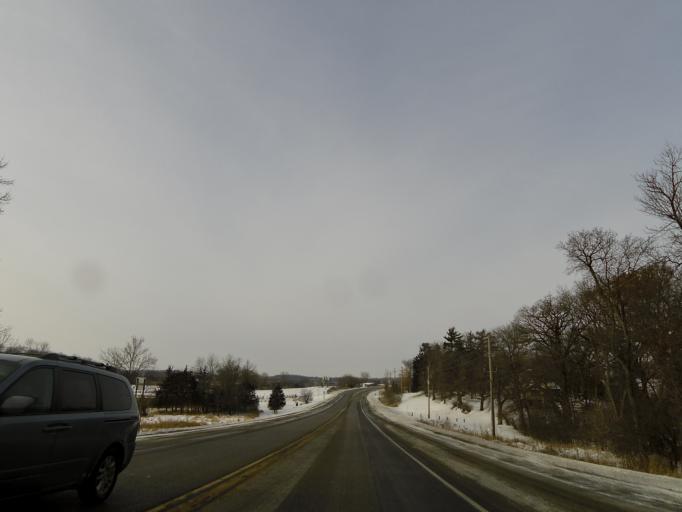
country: US
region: Minnesota
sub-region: Hennepin County
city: Saint Bonifacius
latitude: 44.8986
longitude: -93.7237
